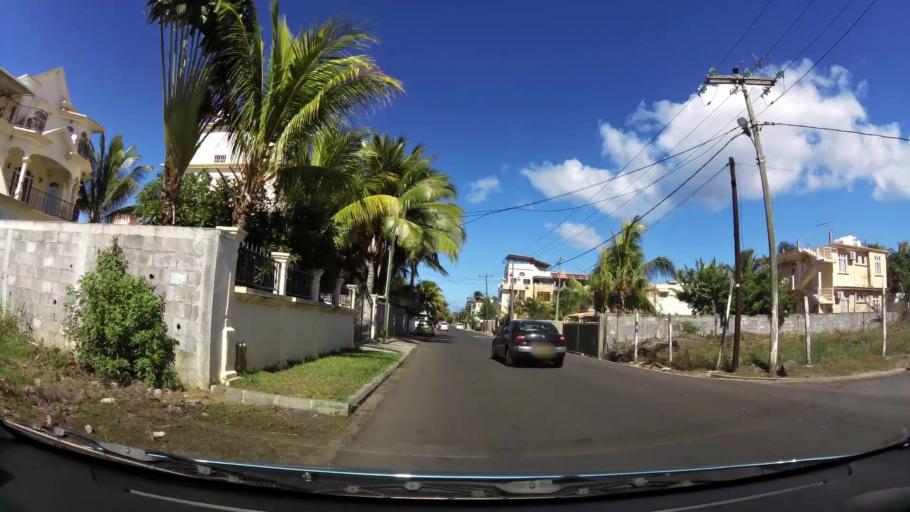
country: MU
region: Black River
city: Flic en Flac
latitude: -20.2859
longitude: 57.3674
